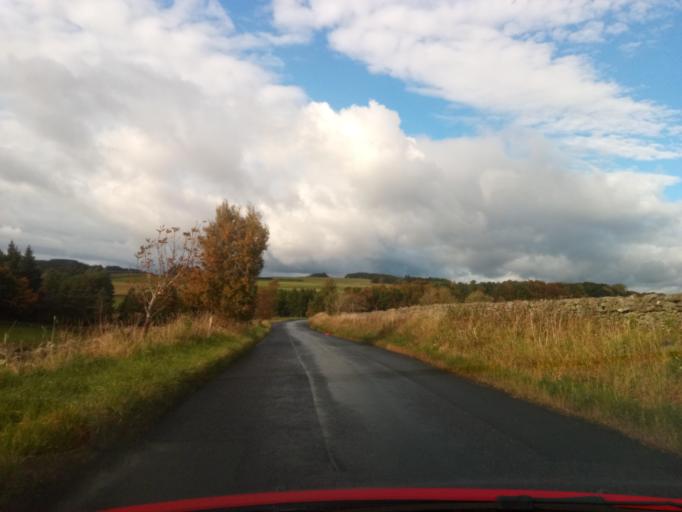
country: GB
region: Scotland
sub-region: The Scottish Borders
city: Galashiels
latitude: 55.6693
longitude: -2.7877
